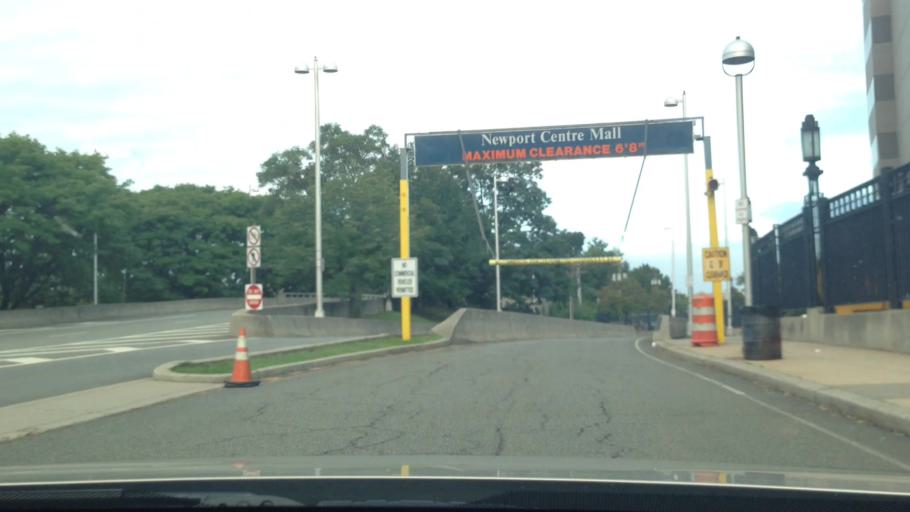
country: US
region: New Jersey
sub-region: Hudson County
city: Hoboken
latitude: 40.7295
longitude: -74.0383
